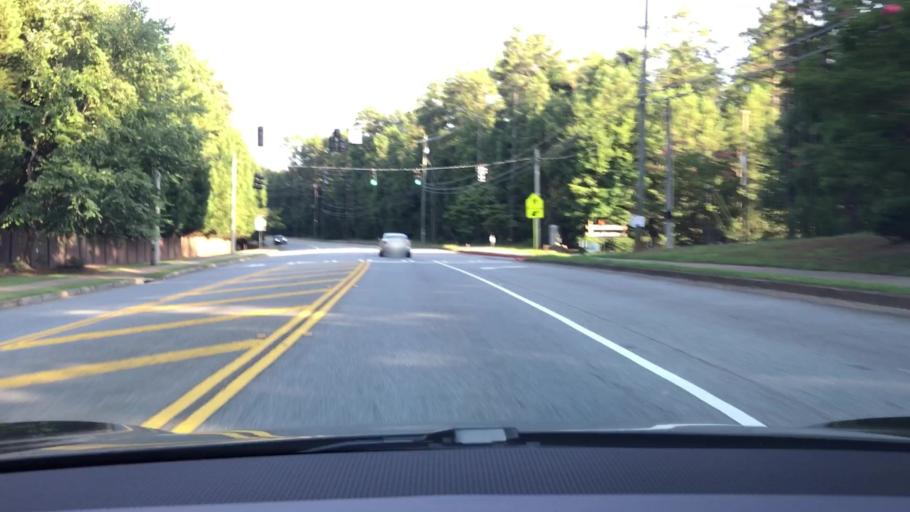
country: US
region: Georgia
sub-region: Fulton County
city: Johns Creek
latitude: 34.0672
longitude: -84.2298
